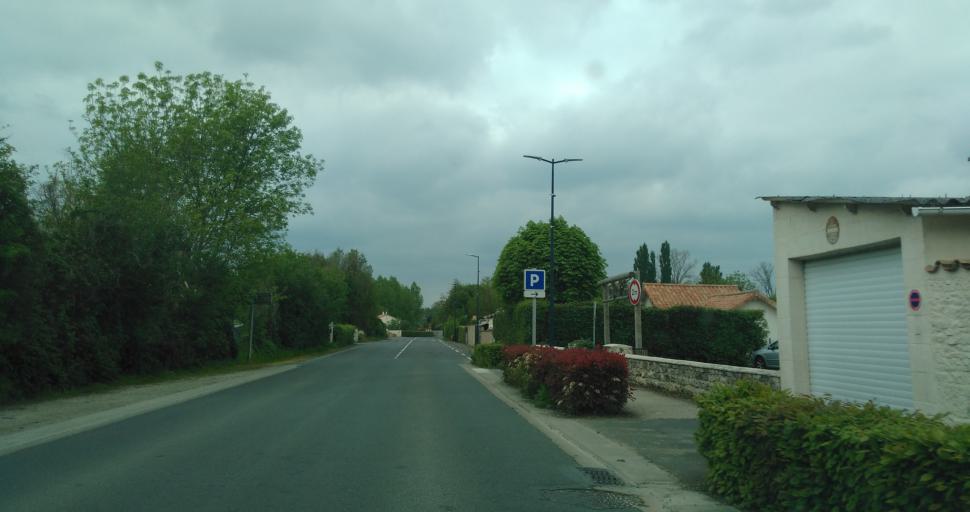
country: FR
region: Poitou-Charentes
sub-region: Departement des Deux-Sevres
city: Bessines
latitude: 46.3112
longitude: -0.5283
